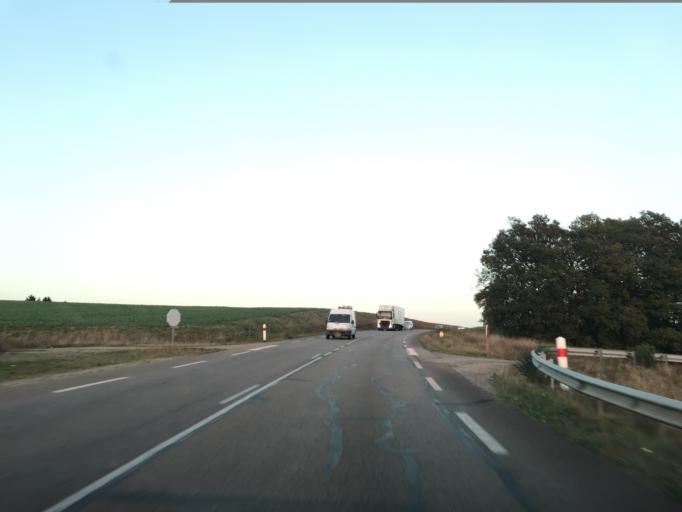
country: FR
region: Haute-Normandie
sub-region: Departement de l'Eure
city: Verneuil-sur-Avre
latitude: 48.7178
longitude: 0.8667
